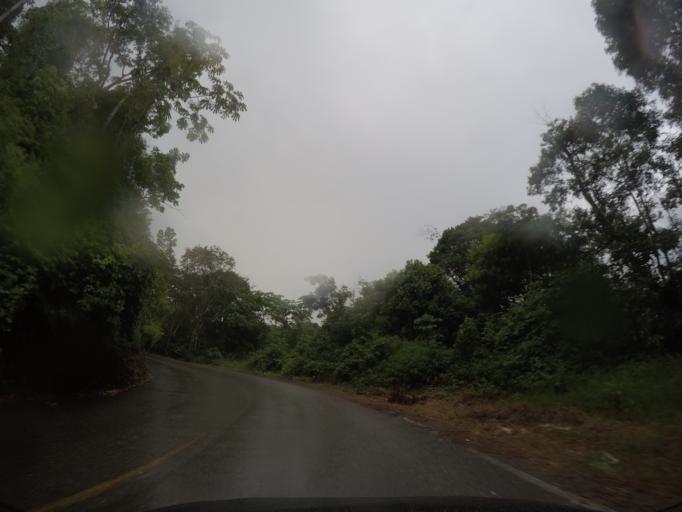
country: MX
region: Oaxaca
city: San Gabriel Mixtepec
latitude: 16.0814
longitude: -97.0801
